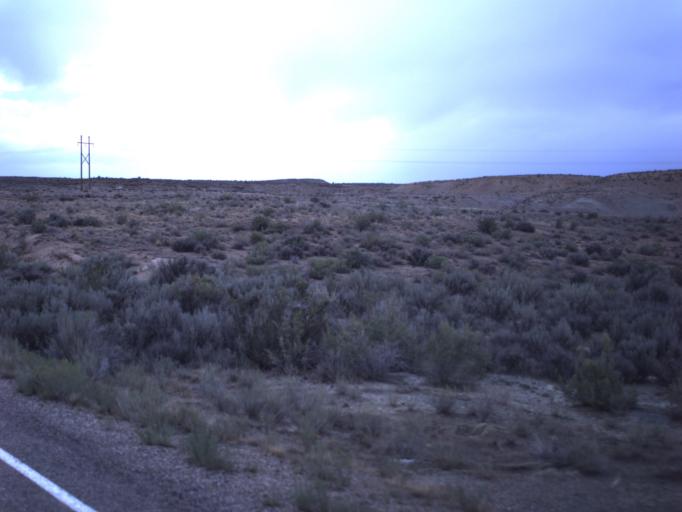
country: US
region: Colorado
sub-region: Rio Blanco County
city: Rangely
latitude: 40.0716
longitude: -109.2042
